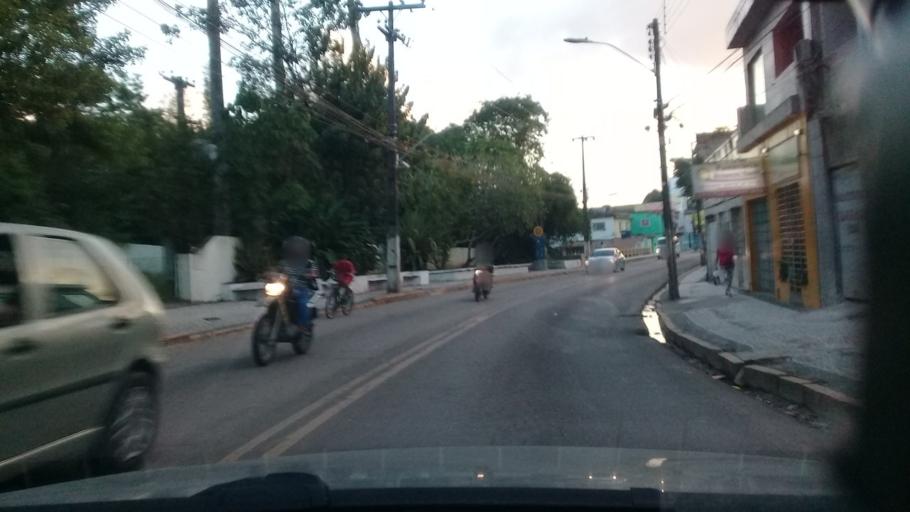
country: BR
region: Pernambuco
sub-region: Jaboatao Dos Guararapes
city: Jaboatao dos Guararapes
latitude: -8.1117
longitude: -35.0129
